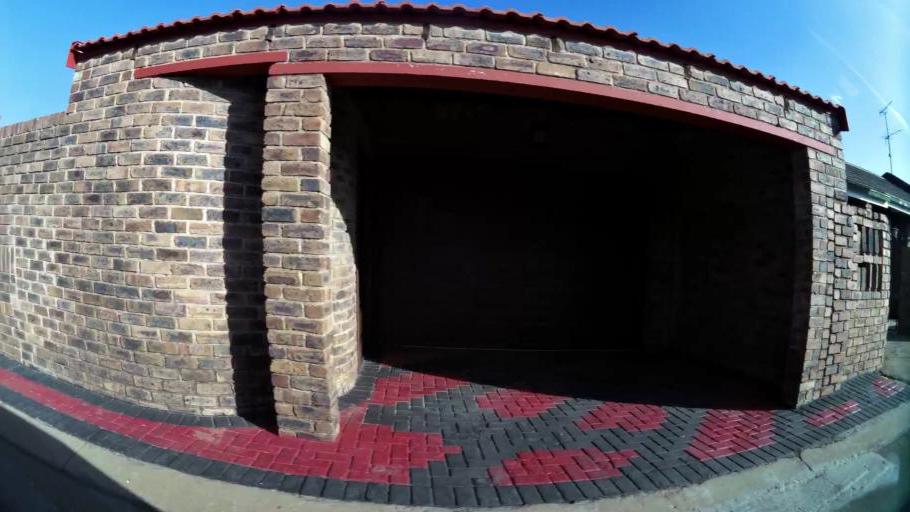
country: ZA
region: Gauteng
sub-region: City of Johannesburg Metropolitan Municipality
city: Soweto
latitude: -26.2758
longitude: 27.9116
